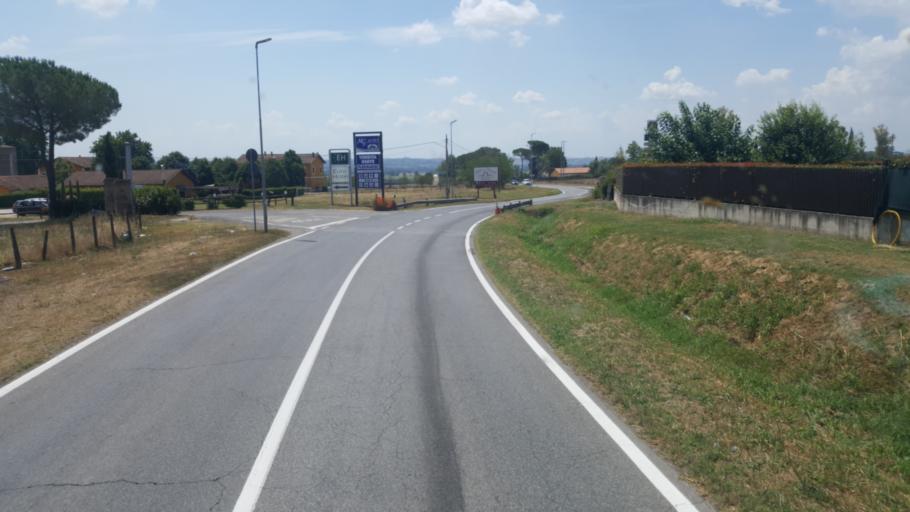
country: IT
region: Latium
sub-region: Citta metropolitana di Roma Capitale
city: Bivio di Capanelle
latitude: 42.1349
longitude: 12.5980
